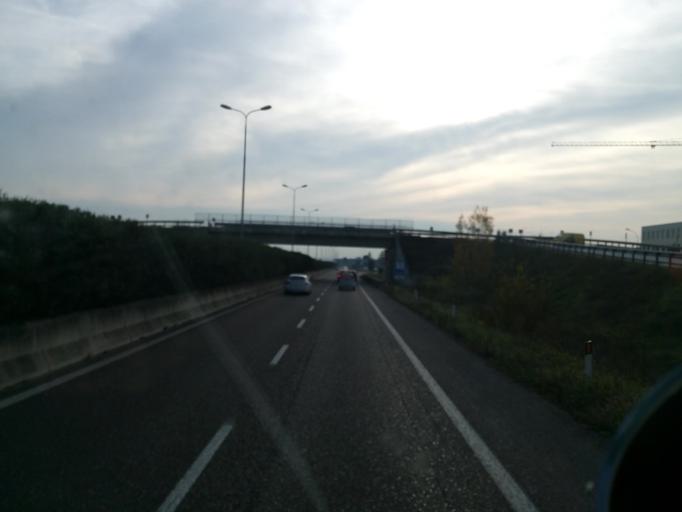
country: IT
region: Lombardy
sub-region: Provincia di Brescia
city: Desenzano del Garda
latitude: 45.4453
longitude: 10.5198
